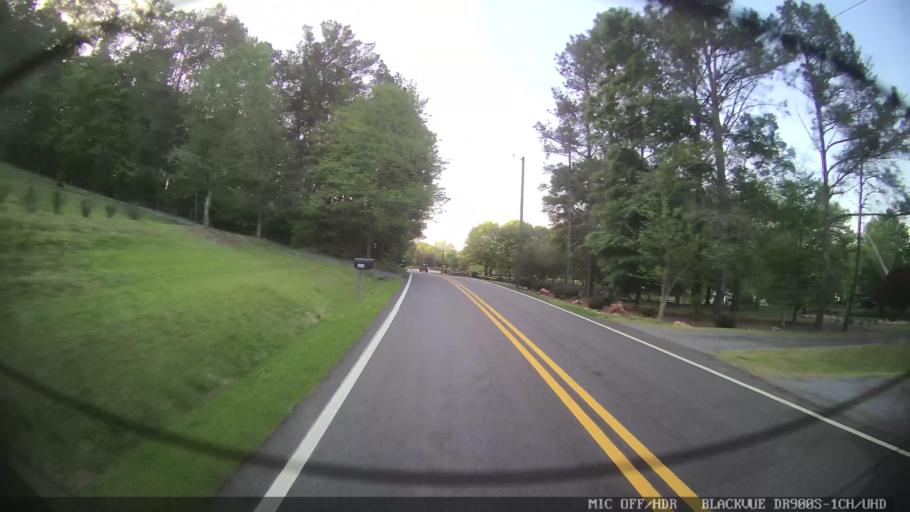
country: US
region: Georgia
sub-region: Bartow County
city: Emerson
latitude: 34.1072
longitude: -84.7861
